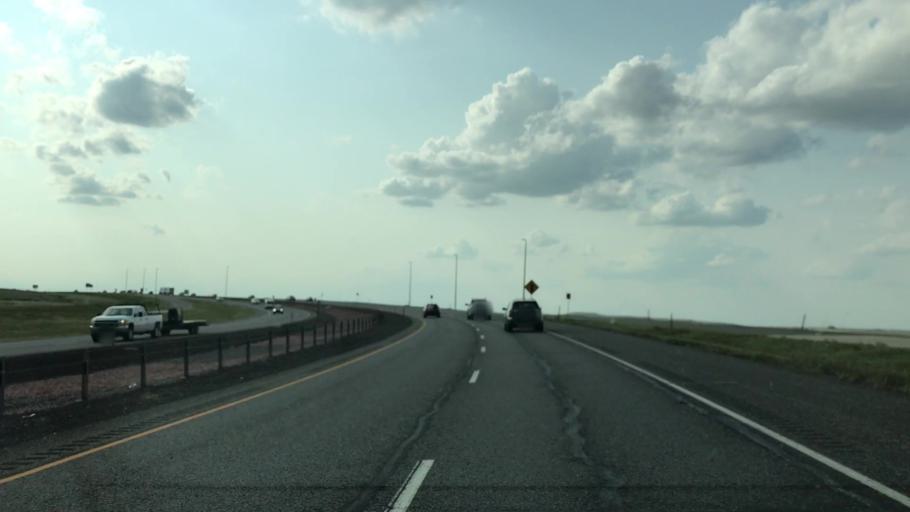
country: US
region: Colorado
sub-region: Adams County
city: Aurora
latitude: 39.8153
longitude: -104.7228
